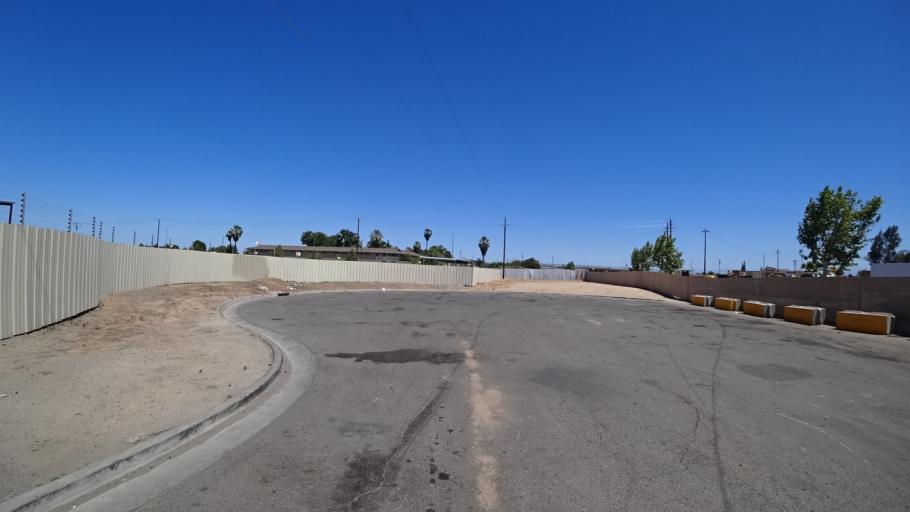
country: US
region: California
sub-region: Fresno County
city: West Park
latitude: 36.7677
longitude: -119.8378
